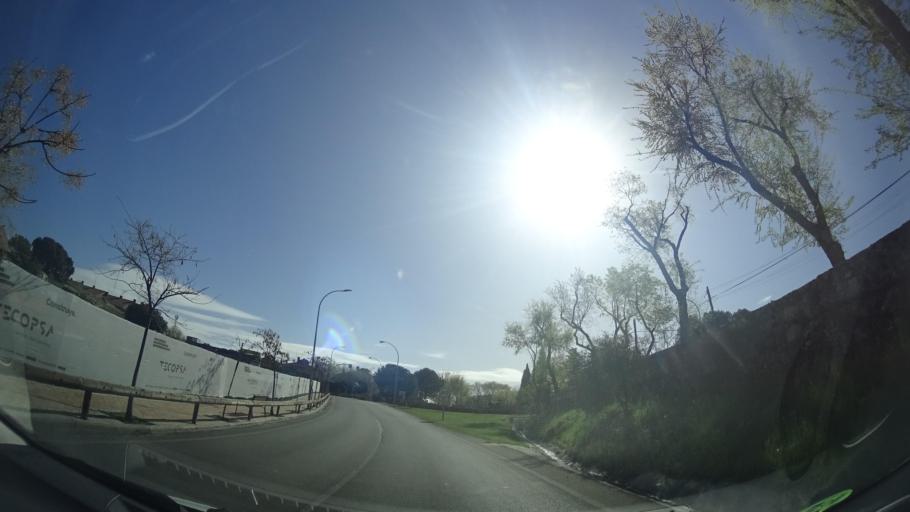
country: ES
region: Madrid
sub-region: Provincia de Madrid
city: Colmenar Viejo
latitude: 40.6542
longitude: -3.7775
